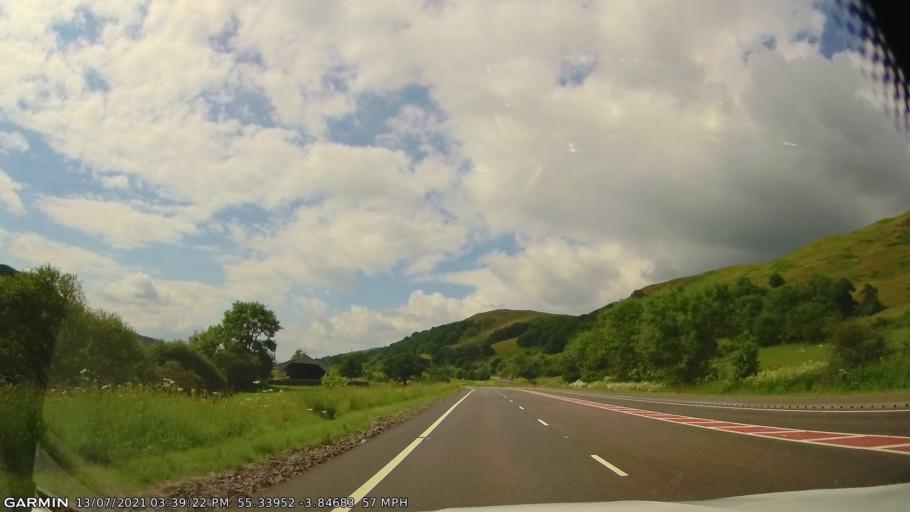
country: GB
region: Scotland
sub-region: Dumfries and Galloway
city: Sanquhar
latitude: 55.3389
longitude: -3.8459
